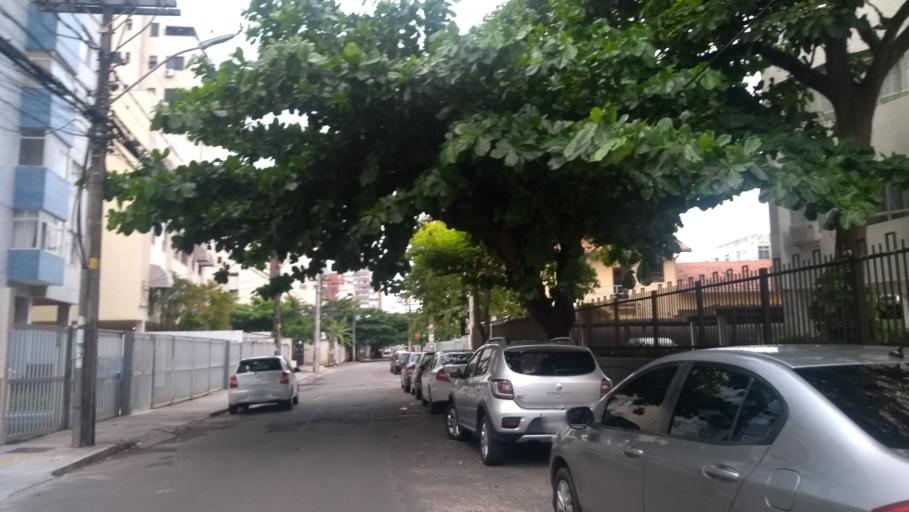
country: BR
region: Bahia
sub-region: Salvador
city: Salvador
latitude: -12.9907
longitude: -38.4472
